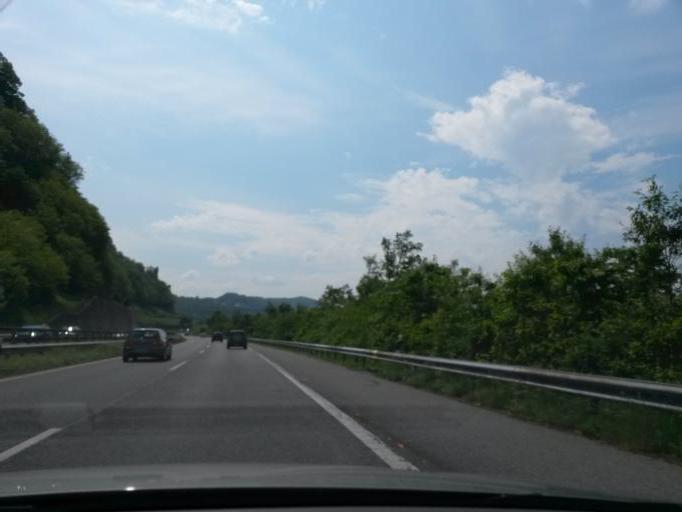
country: CH
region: Ticino
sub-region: Lugano District
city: Bioggio
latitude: 46.0064
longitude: 8.9148
